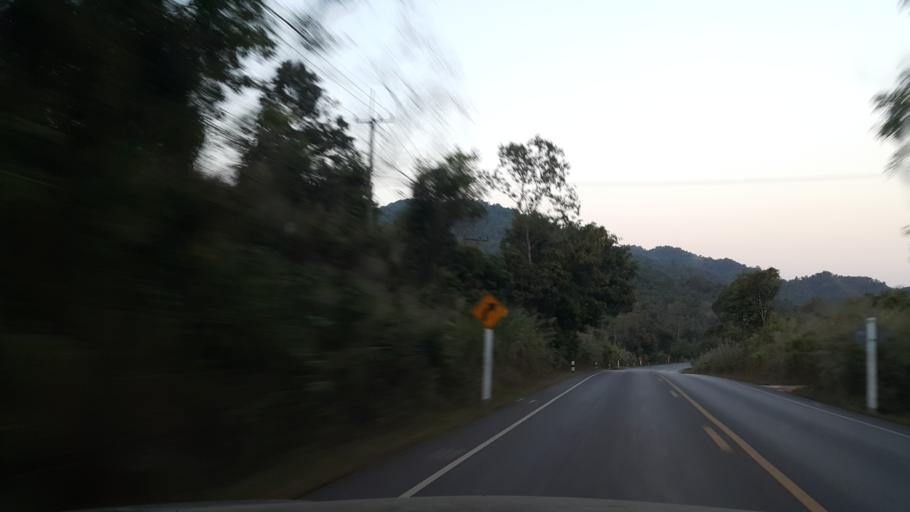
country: TH
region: Phrae
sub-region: Amphoe Wang Chin
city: Wang Chin
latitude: 17.9683
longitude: 99.6161
